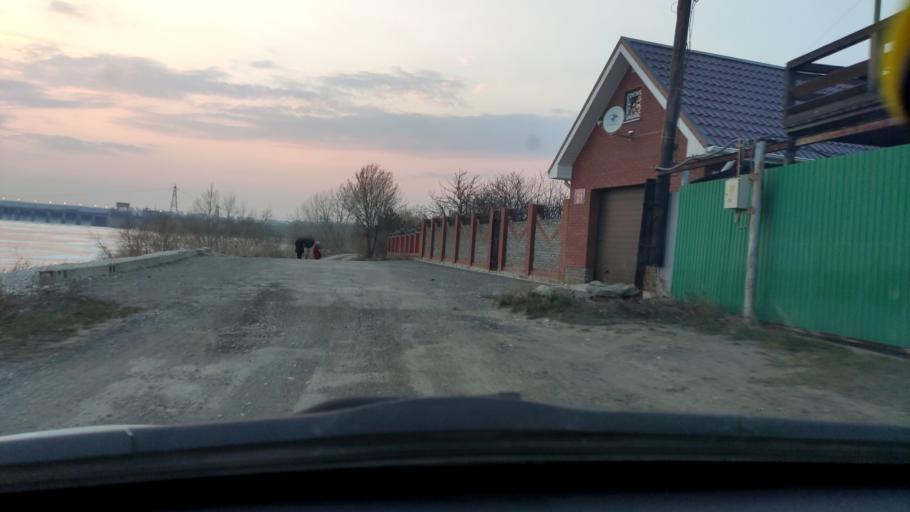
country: RU
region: Samara
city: Zhigulevsk
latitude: 53.4532
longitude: 49.5201
